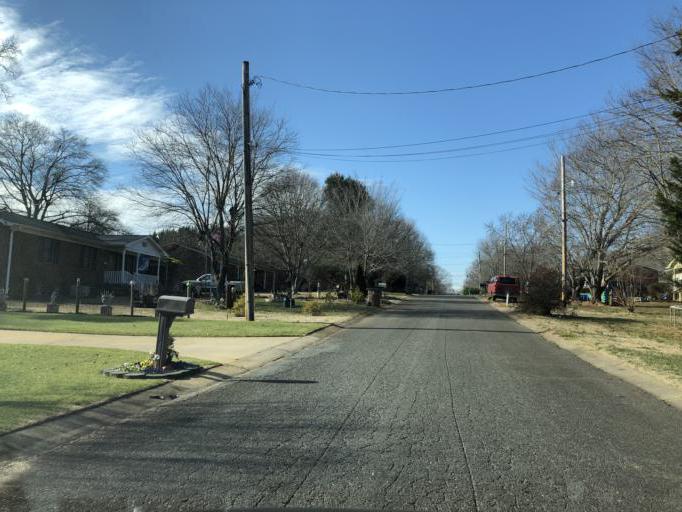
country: US
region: North Carolina
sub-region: Cleveland County
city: Shelby
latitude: 35.2689
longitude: -81.5450
